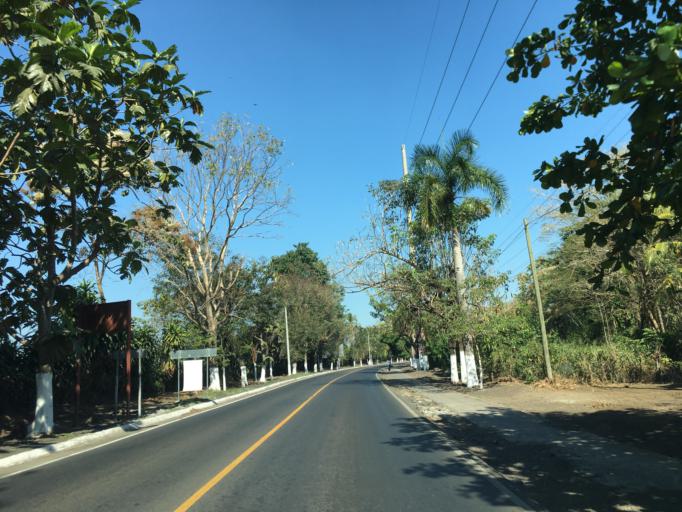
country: GT
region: Escuintla
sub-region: Municipio de La Democracia
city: La Democracia
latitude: 14.2356
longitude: -90.9522
